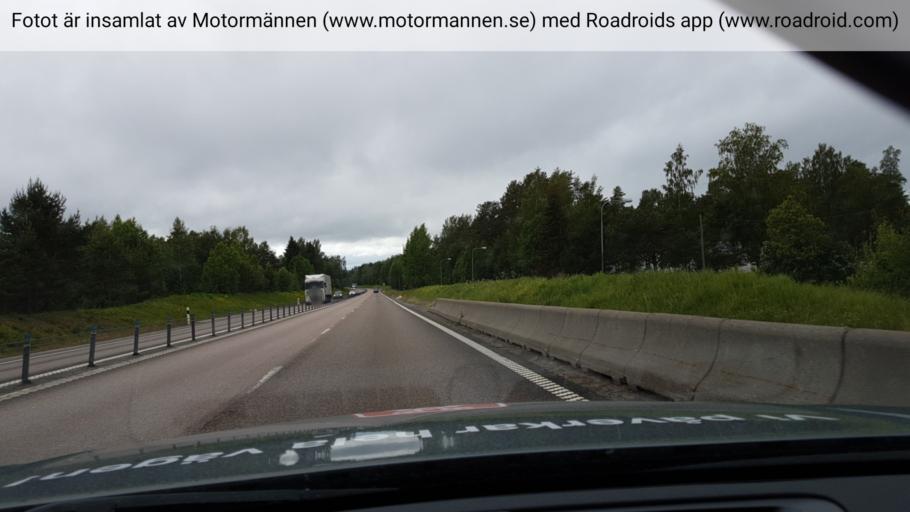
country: SE
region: Vaesternorrland
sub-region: Timra Kommun
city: Bergeforsen
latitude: 62.5146
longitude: 17.3830
